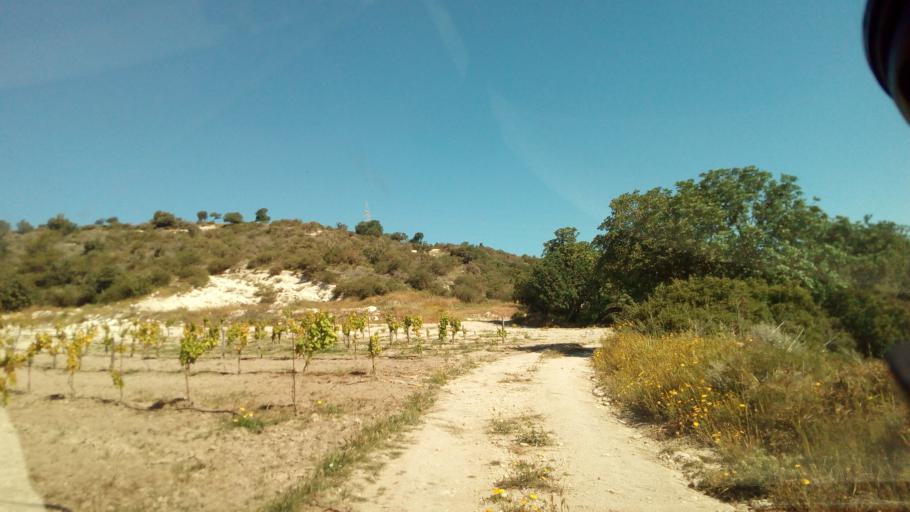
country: CY
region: Limassol
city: Pissouri
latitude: 34.6756
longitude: 32.6885
